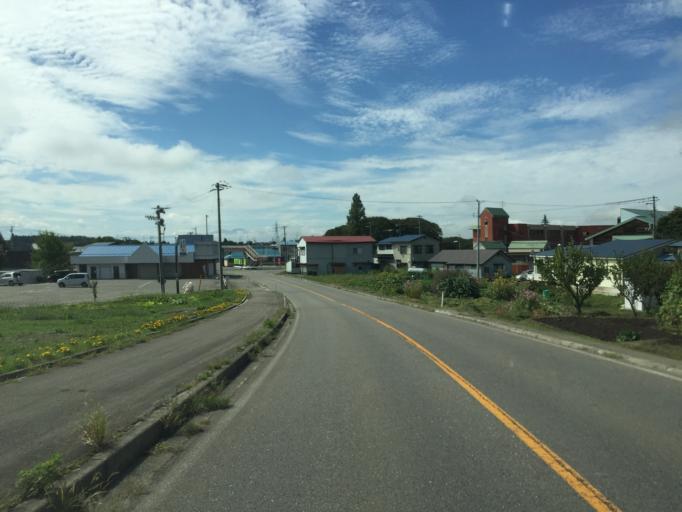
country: JP
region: Fukushima
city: Inawashiro
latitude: 37.5606
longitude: 139.9888
